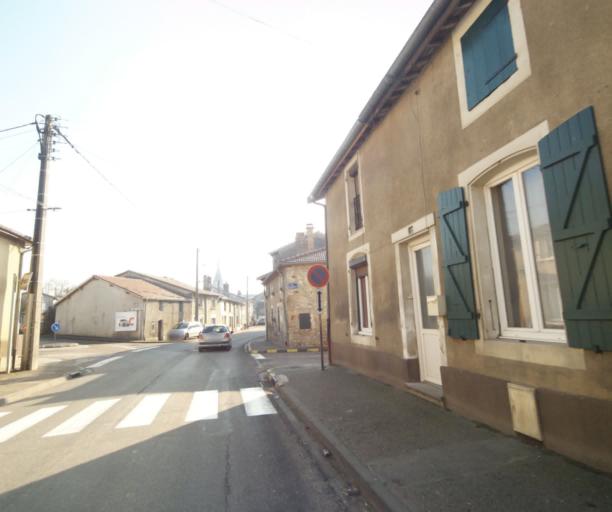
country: FR
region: Champagne-Ardenne
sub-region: Departement de la Haute-Marne
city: Wassy
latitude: 48.5019
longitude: 4.9466
